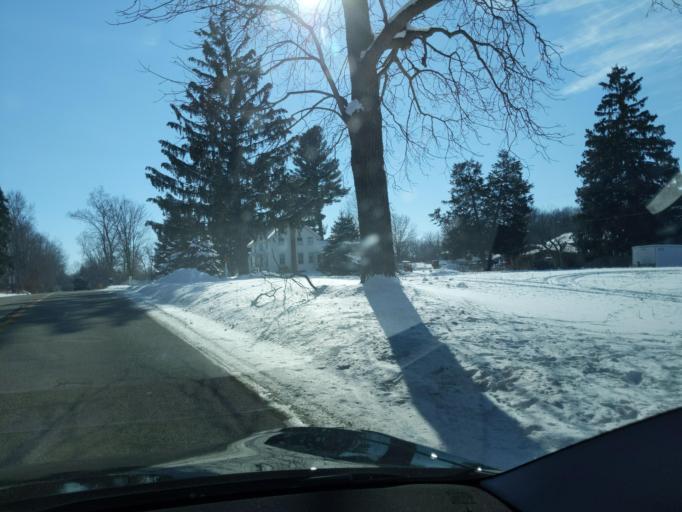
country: US
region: Michigan
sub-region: Ingham County
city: Stockbridge
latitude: 42.4510
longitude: -84.0765
